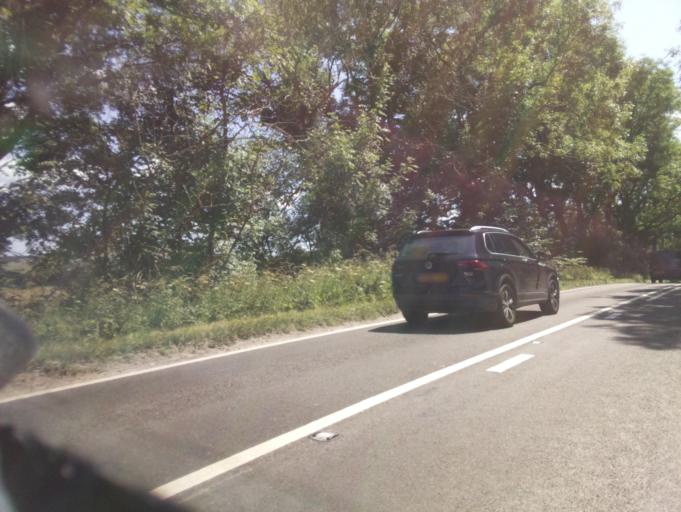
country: GB
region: England
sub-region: Derbyshire
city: Buxton
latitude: 53.2274
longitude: -1.8751
